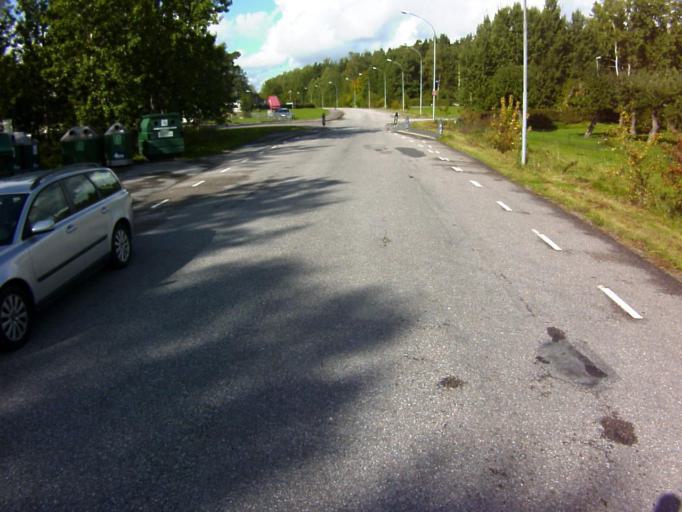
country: SE
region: Soedermanland
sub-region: Eskilstuna Kommun
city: Eskilstuna
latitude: 59.3964
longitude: 16.5426
